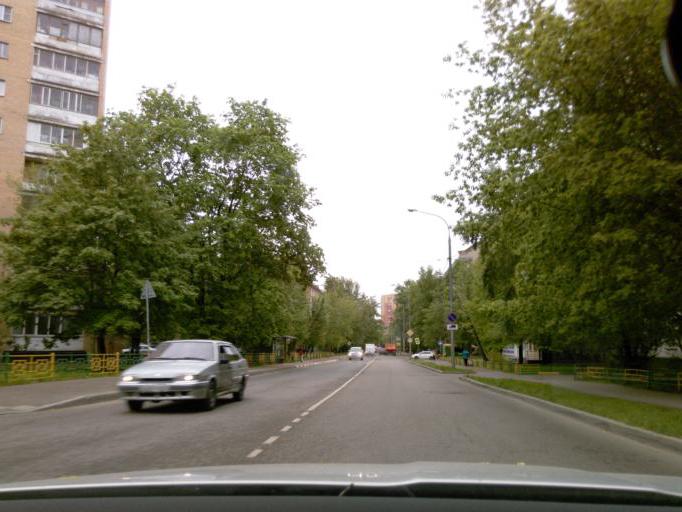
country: RU
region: Moscow
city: Zapadnoye Degunino
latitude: 55.8598
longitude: 37.5186
